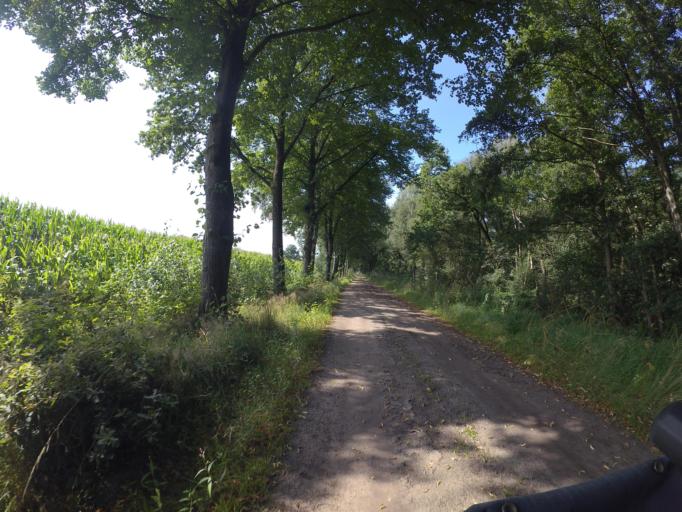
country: NL
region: North Brabant
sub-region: Bergeijk
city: Bergeyk
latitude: 51.3645
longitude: 5.3650
